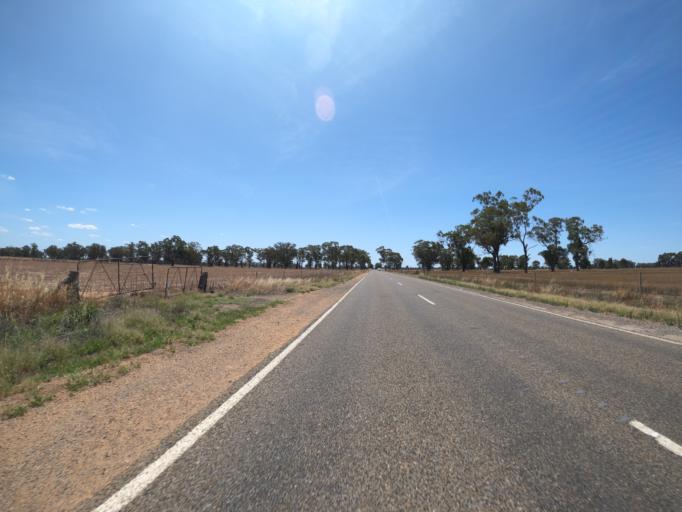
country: AU
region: Victoria
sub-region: Moira
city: Yarrawonga
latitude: -36.1814
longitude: 145.9672
